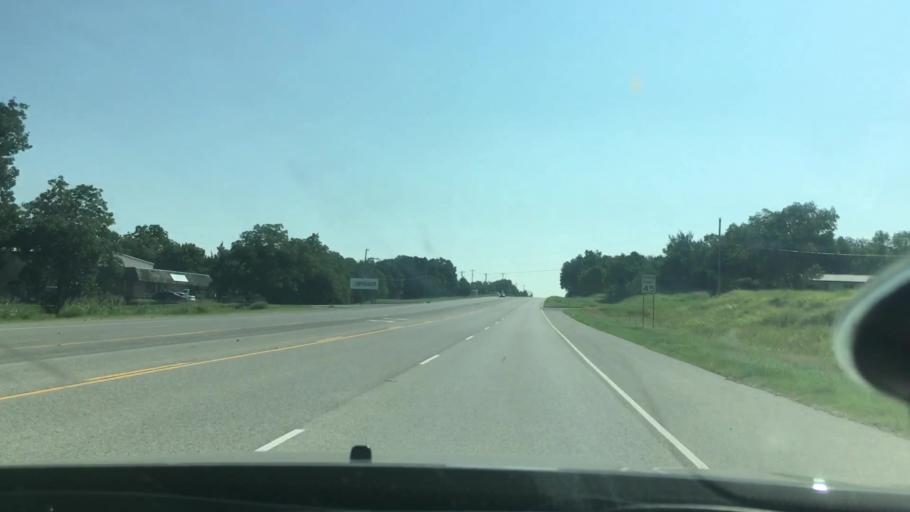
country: US
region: Oklahoma
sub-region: Marshall County
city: Oakland
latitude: 34.0999
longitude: -96.8038
